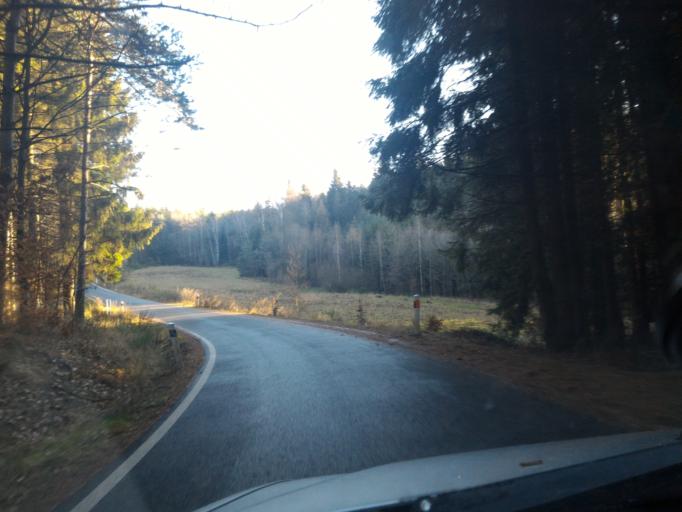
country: DE
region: Saxony
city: Kurort Jonsdorf
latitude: 50.8195
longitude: 14.7037
